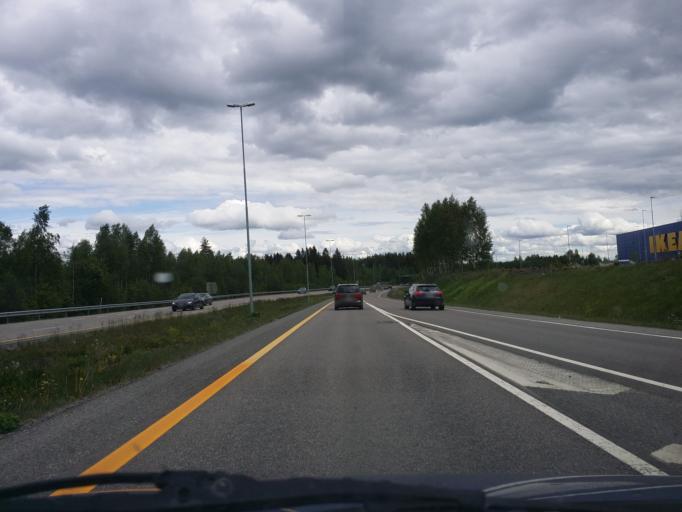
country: NO
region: Hedmark
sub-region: Hamar
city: Hamar
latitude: 60.8419
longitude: 11.0550
